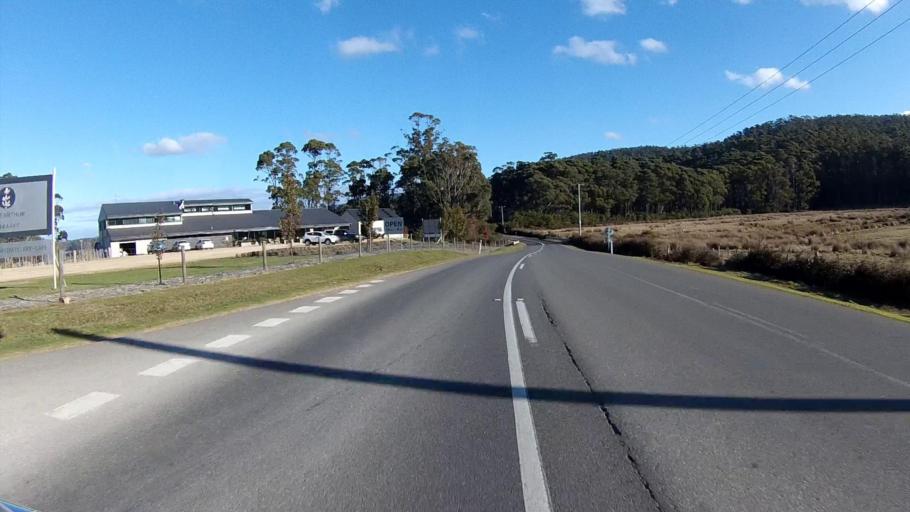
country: AU
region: Tasmania
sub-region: Clarence
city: Sandford
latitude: -43.1060
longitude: 147.8635
